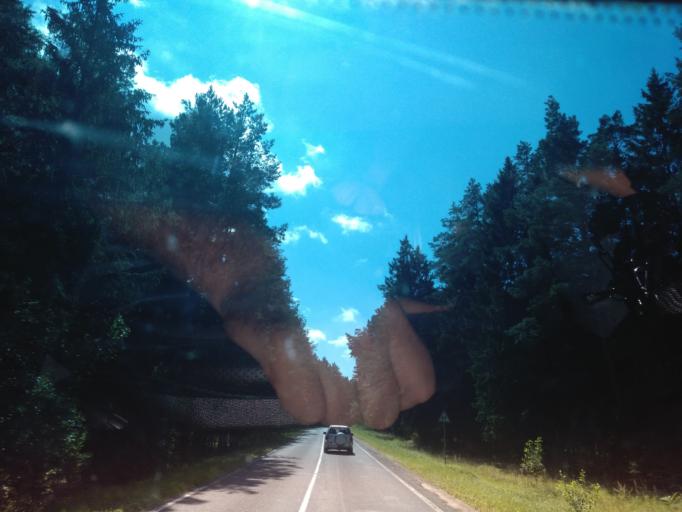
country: BY
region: Minsk
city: Uzda
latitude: 53.2980
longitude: 27.2385
